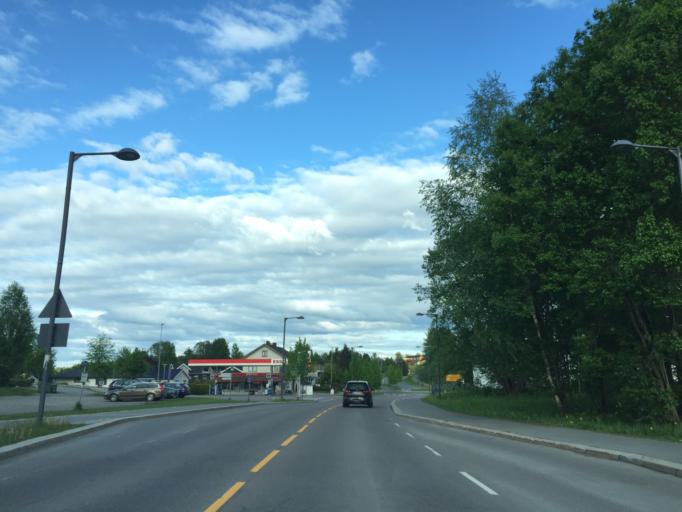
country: NO
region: Akershus
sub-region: Sorum
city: Sorumsand
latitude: 59.9868
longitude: 11.2485
